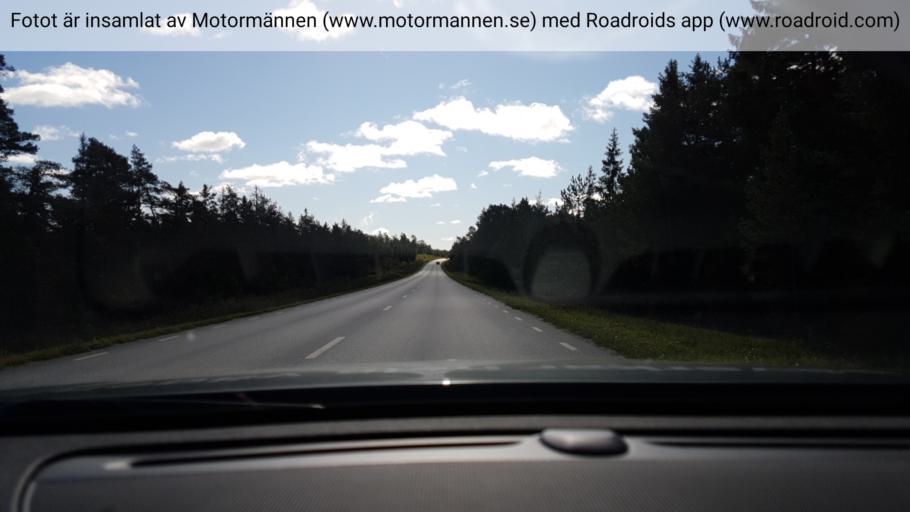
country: SE
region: Gotland
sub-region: Gotland
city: Slite
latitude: 57.7434
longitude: 18.7896
